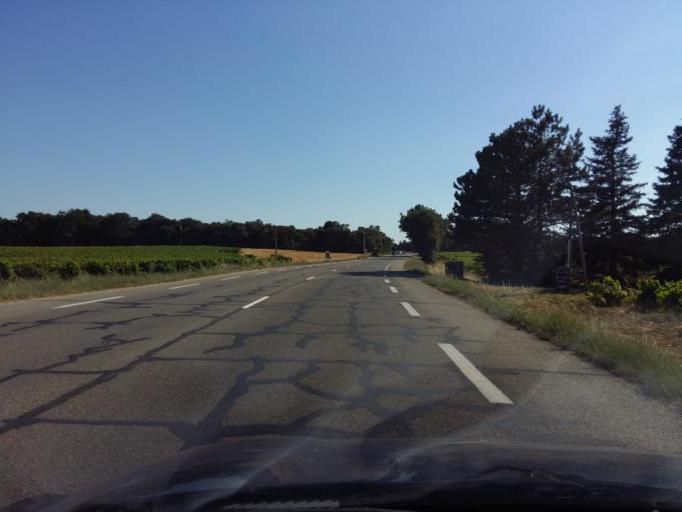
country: FR
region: Provence-Alpes-Cote d'Azur
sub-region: Departement du Vaucluse
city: Visan
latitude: 44.3448
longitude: 4.9534
